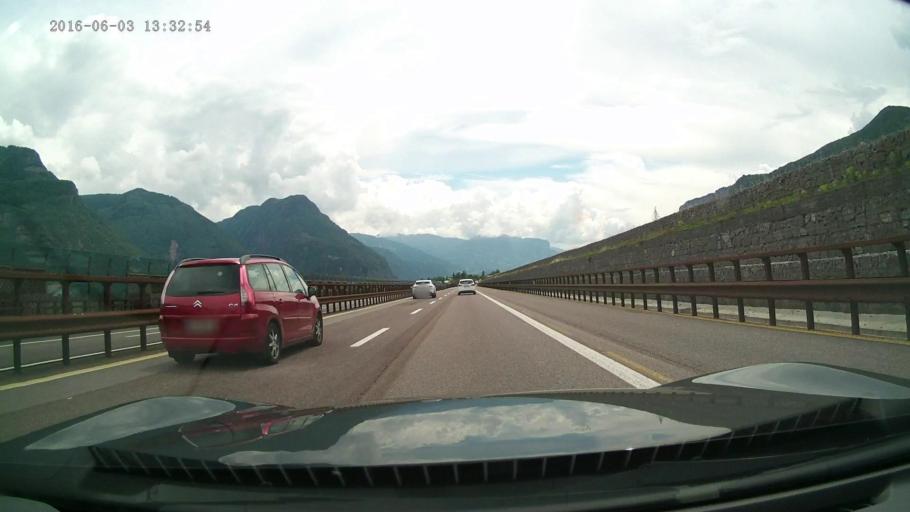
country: IT
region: Trentino-Alto Adige
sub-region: Bolzano
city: Vadena
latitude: 46.4279
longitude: 11.3158
